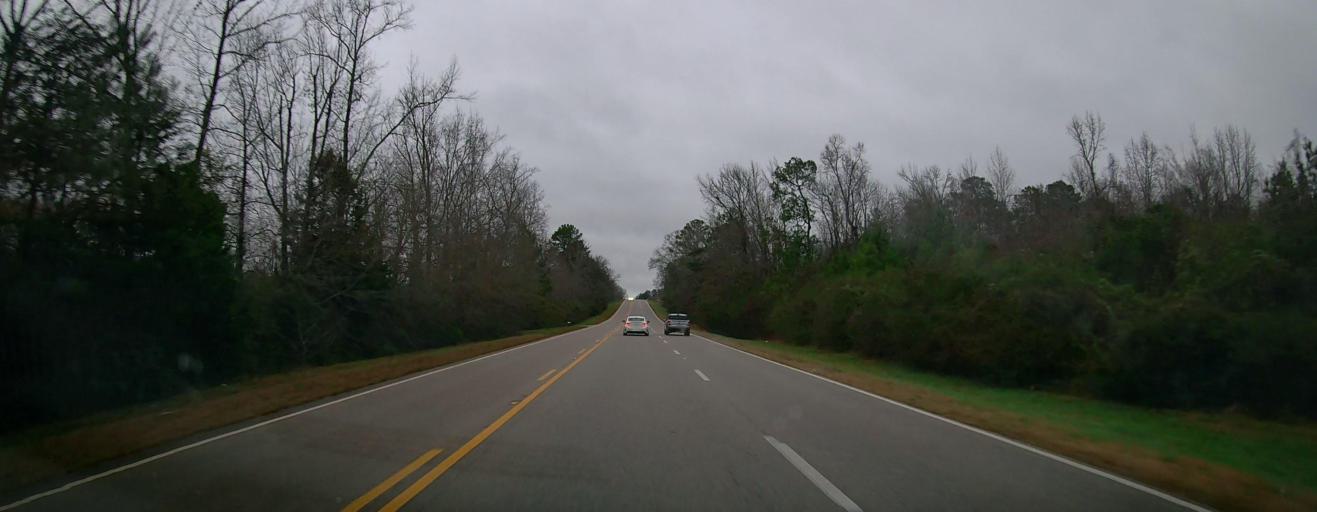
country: US
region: Alabama
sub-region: Bibb County
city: Centreville
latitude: 32.8511
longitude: -86.9626
